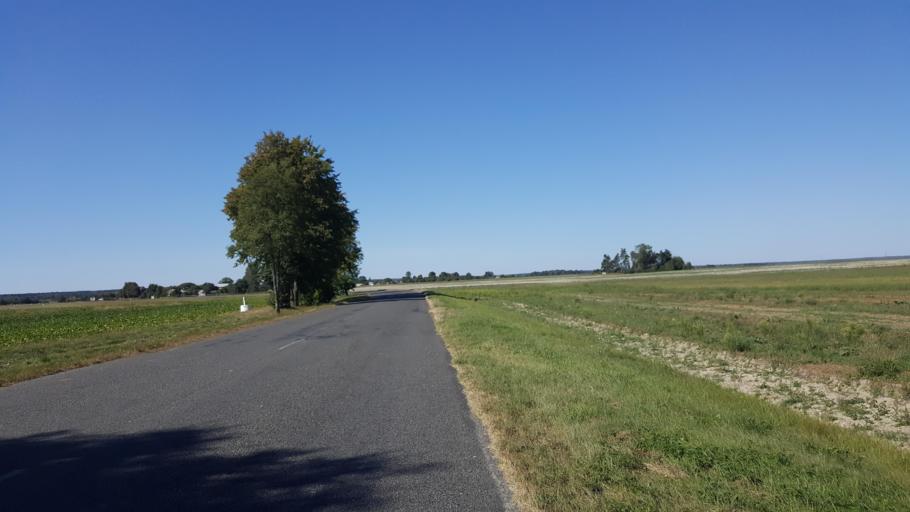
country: BY
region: Brest
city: Charnawchytsy
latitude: 52.2612
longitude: 23.5520
